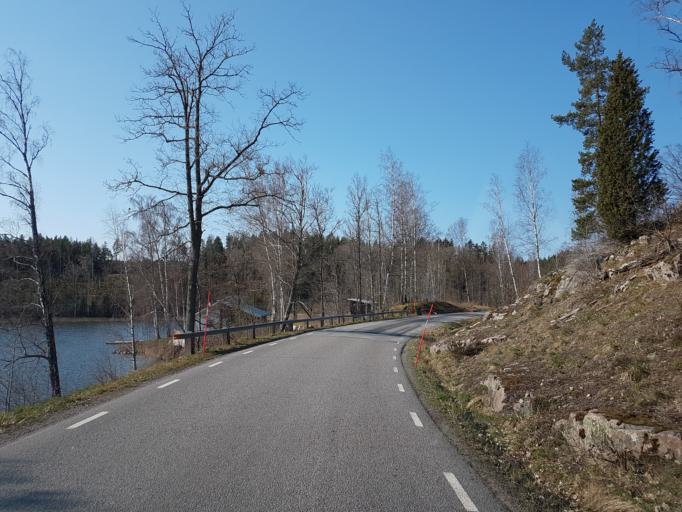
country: SE
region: OEstergoetland
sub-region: Valdemarsviks Kommun
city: Gusum
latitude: 58.1924
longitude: 16.3153
